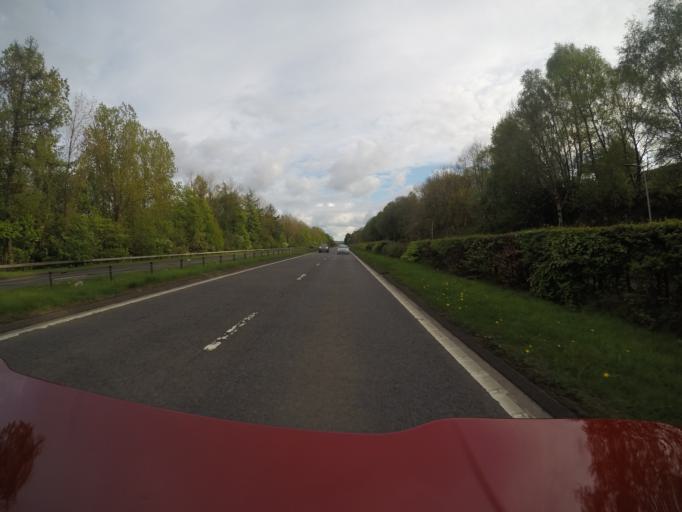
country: GB
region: Scotland
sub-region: West Dunbartonshire
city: Renton
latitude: 55.9737
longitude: -4.5877
